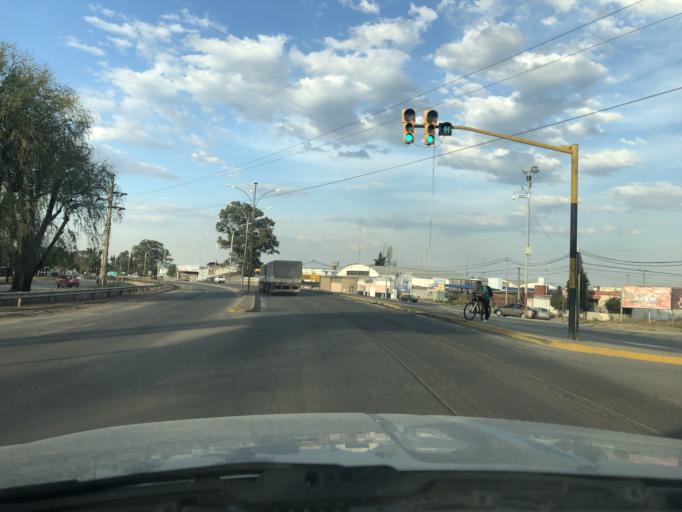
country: AR
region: Cordoba
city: Jesus Maria
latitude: -30.9873
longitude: -64.0903
